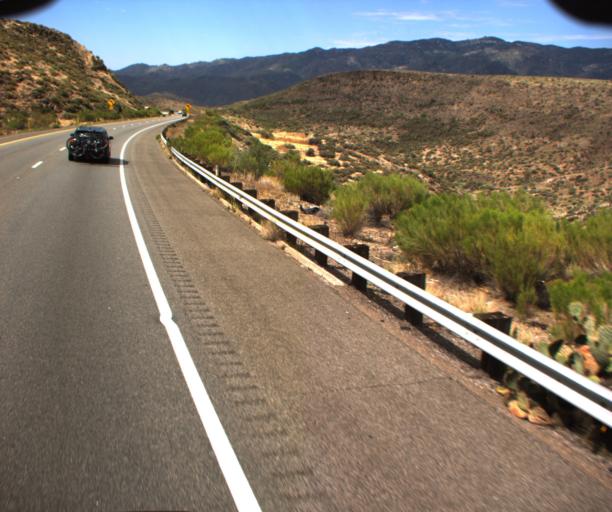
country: US
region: Arizona
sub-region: Yavapai County
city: Black Canyon City
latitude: 34.1667
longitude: -112.1438
